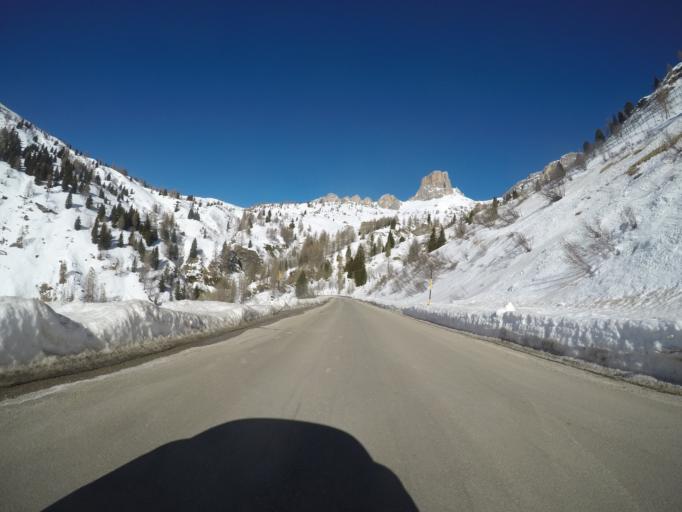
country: IT
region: Veneto
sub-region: Provincia di Belluno
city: Selva di Cadore
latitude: 46.4823
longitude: 12.0354
